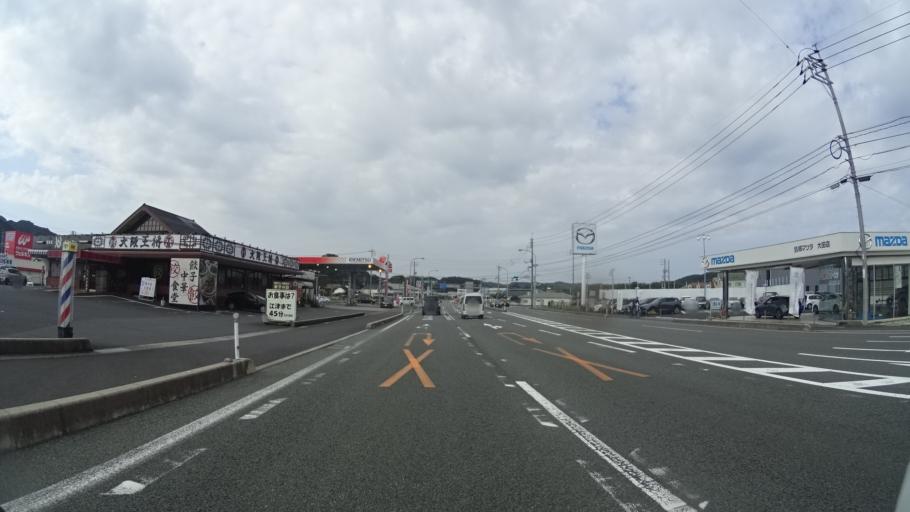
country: JP
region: Shimane
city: Odacho-oda
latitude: 35.1996
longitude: 132.4908
